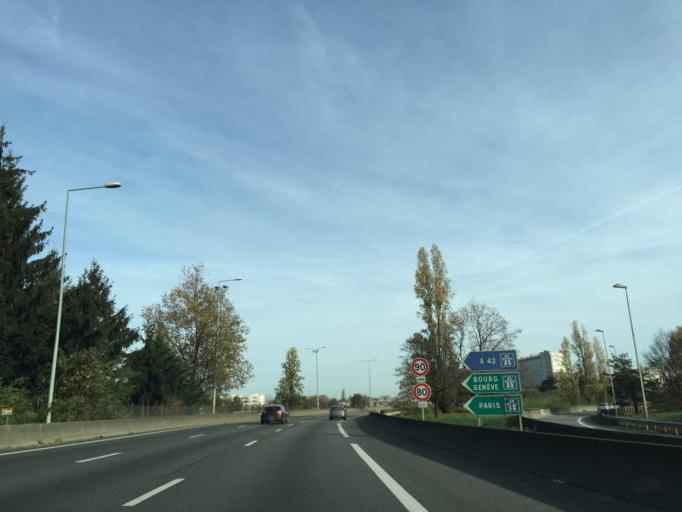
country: FR
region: Rhone-Alpes
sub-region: Departement du Rhone
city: Bron
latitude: 45.7263
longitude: 4.8963
